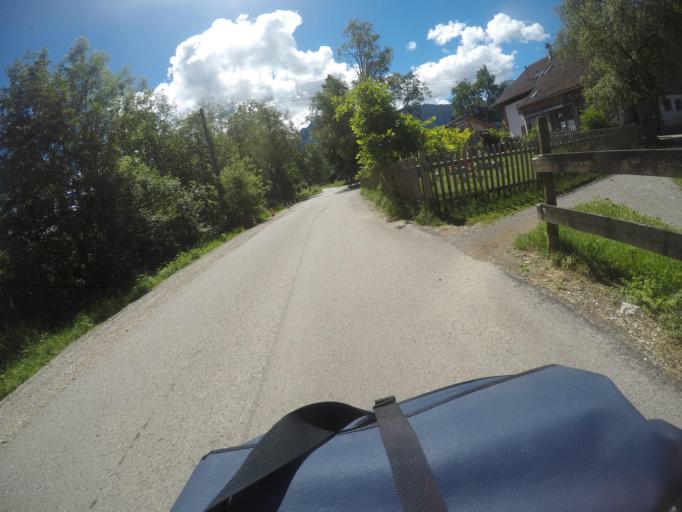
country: DE
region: Bavaria
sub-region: Swabia
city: Schwangau
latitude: 47.5910
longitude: 10.7443
